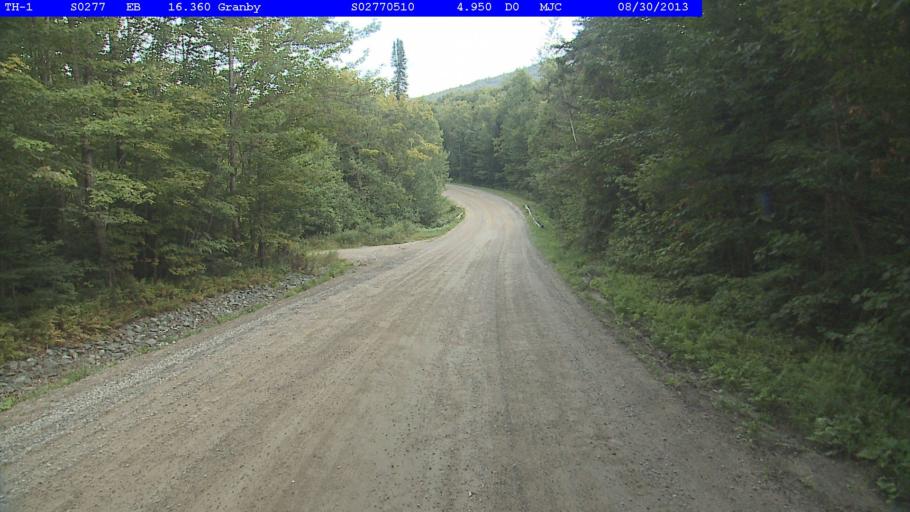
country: US
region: Vermont
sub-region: Essex County
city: Guildhall
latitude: 44.5771
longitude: -71.6748
